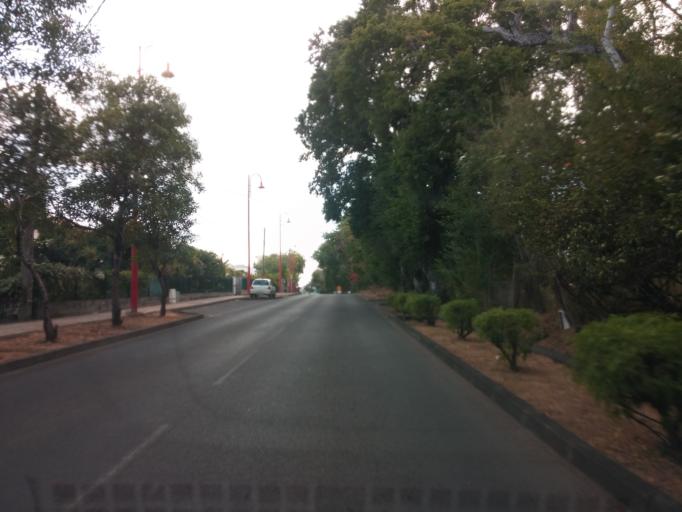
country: RE
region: Reunion
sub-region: Reunion
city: La Possession
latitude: -20.9355
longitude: 55.3337
